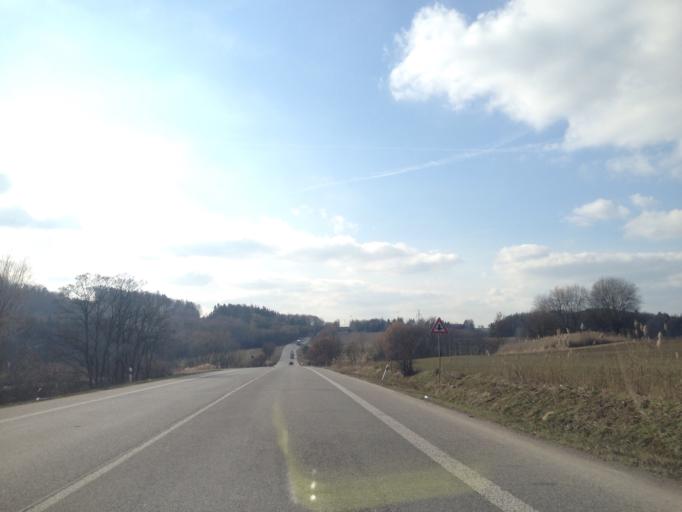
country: CZ
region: Kralovehradecky
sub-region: Okres Jicin
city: Jicin
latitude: 50.4556
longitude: 15.2823
